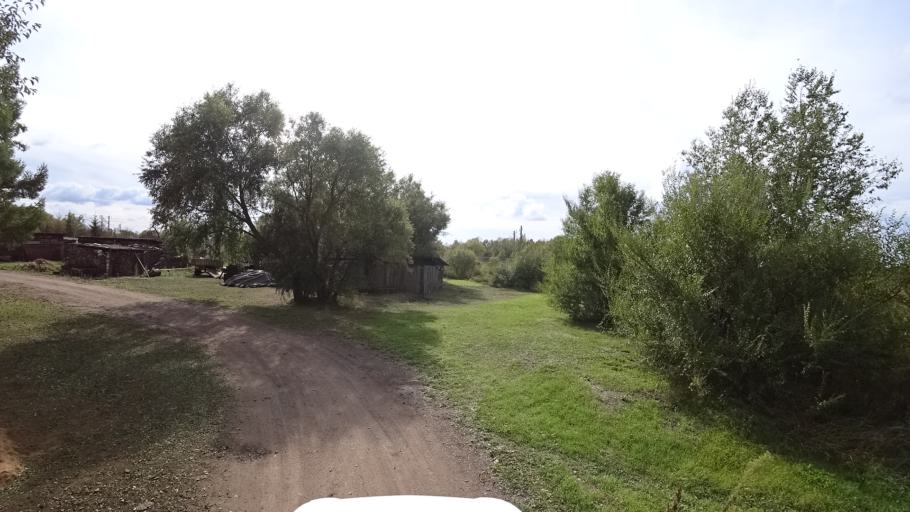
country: RU
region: Amur
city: Arkhara
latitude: 49.3541
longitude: 130.1573
